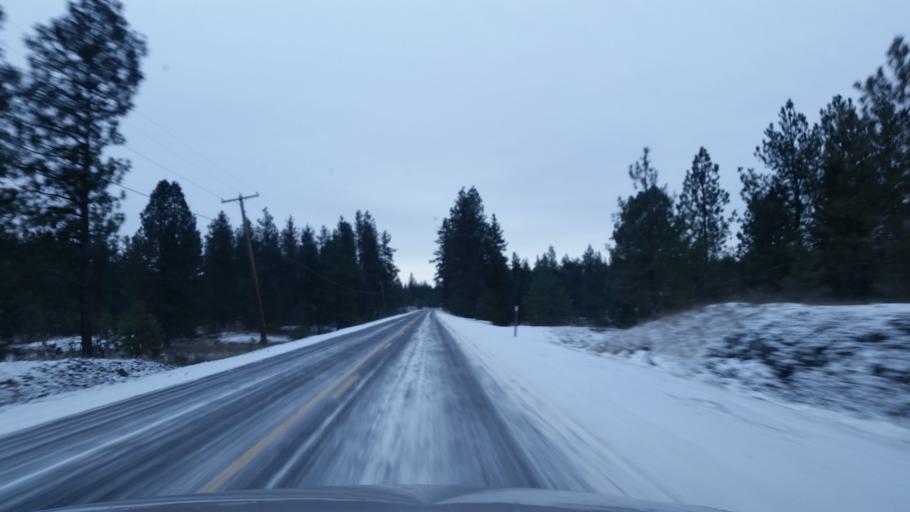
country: US
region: Washington
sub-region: Spokane County
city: Cheney
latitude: 47.4619
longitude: -117.5306
